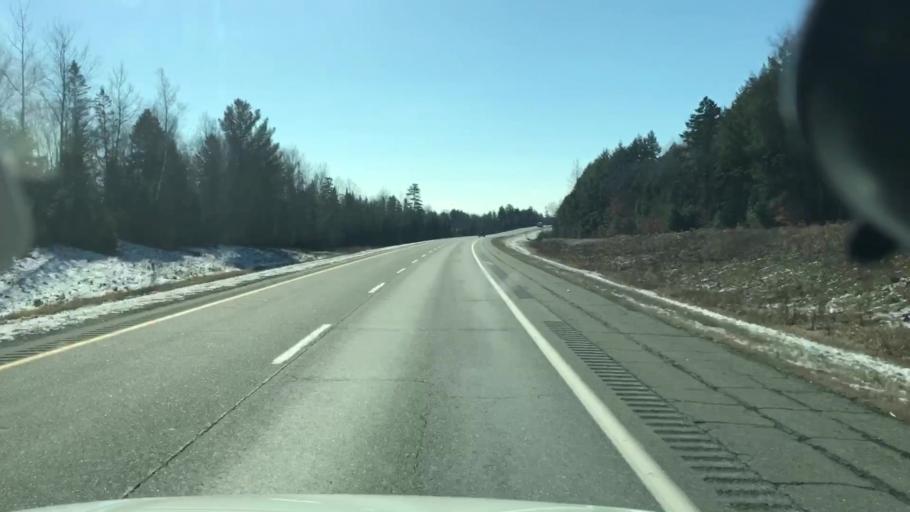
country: US
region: Maine
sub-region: Penobscot County
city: Howland
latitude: 45.2893
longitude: -68.6664
